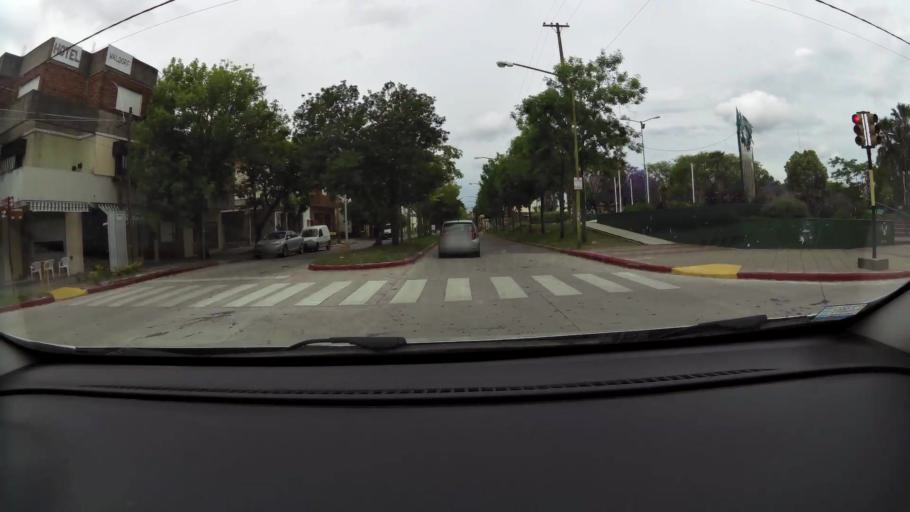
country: AR
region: Buenos Aires
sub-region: Partido de Campana
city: Campana
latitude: -34.1699
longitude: -58.9598
